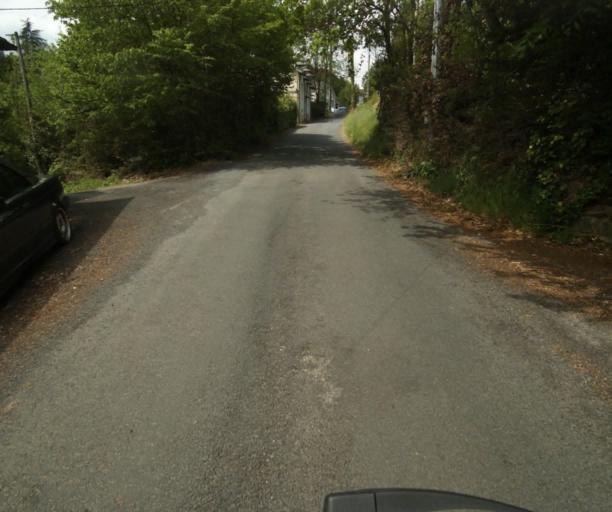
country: FR
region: Limousin
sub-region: Departement de la Correze
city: Tulle
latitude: 45.2710
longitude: 1.7575
